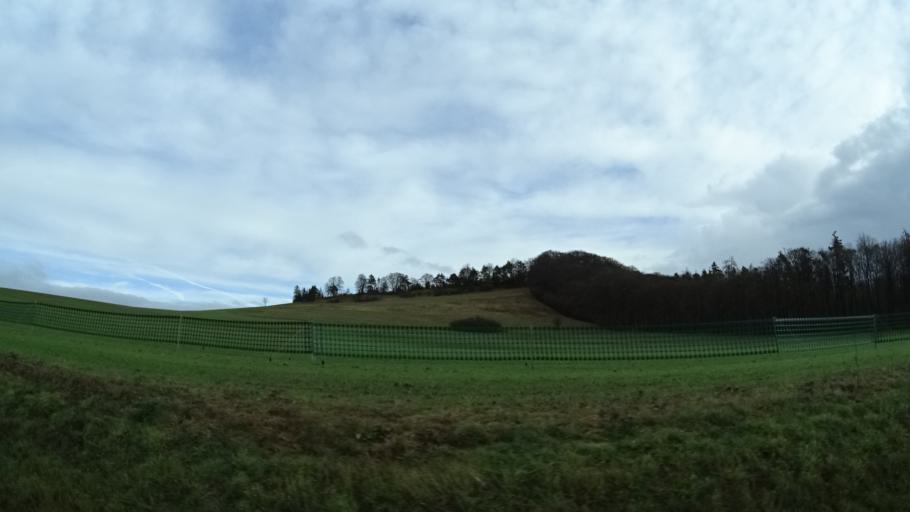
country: DE
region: Thuringia
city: Stepfershausen
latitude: 50.5899
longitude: 10.3145
